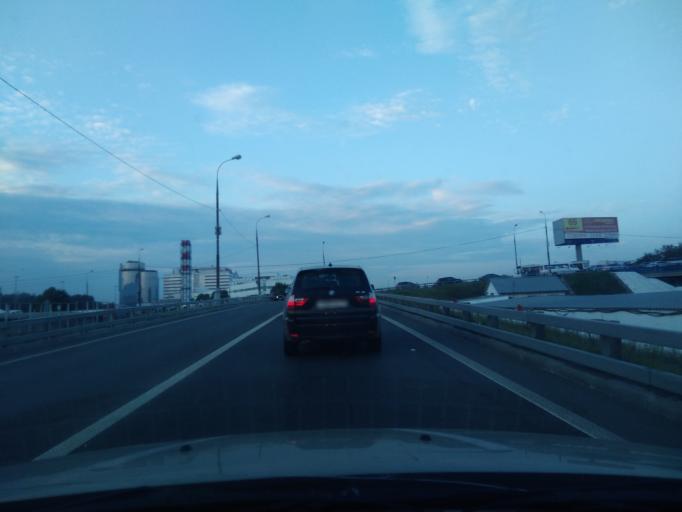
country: RU
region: Moscow
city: Strogino
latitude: 55.8081
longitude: 37.3864
